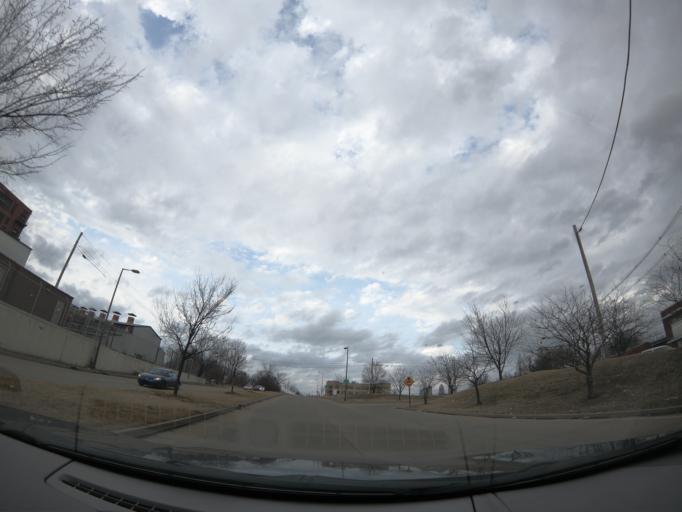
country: US
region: Kentucky
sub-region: Jefferson County
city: Louisville
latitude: 38.2312
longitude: -85.7671
